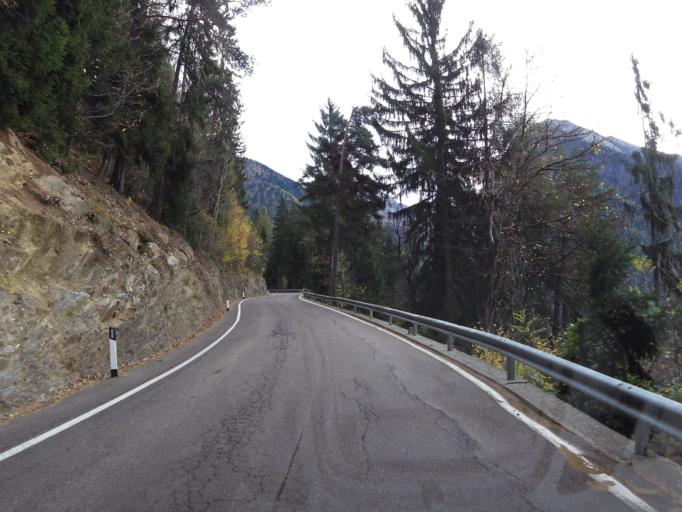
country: IT
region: Trentino-Alto Adige
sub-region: Bolzano
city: San Leonardo in Passiria
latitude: 46.8192
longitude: 11.2473
